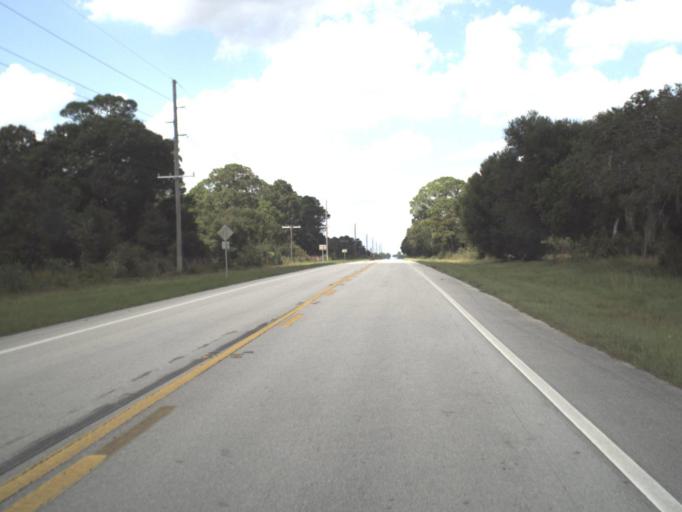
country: US
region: Florida
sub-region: Okeechobee County
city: Okeechobee
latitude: 27.3629
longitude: -81.0583
